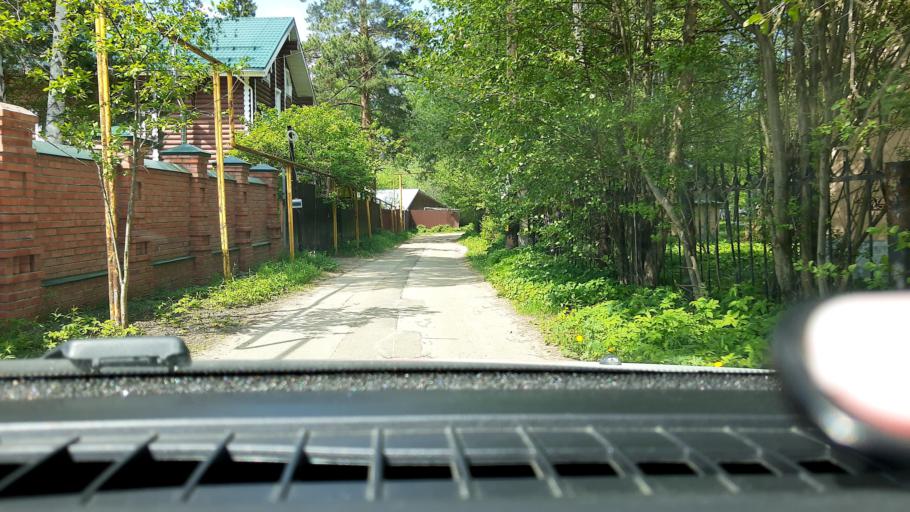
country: RU
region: Nizjnij Novgorod
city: Afonino
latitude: 56.1858
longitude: 44.1006
